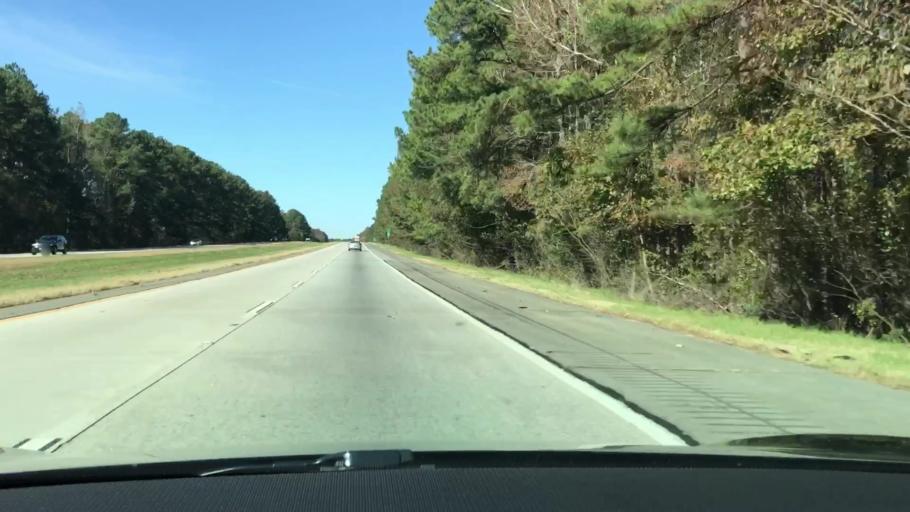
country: US
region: Georgia
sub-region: Greene County
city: Union Point
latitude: 33.5437
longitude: -83.0213
